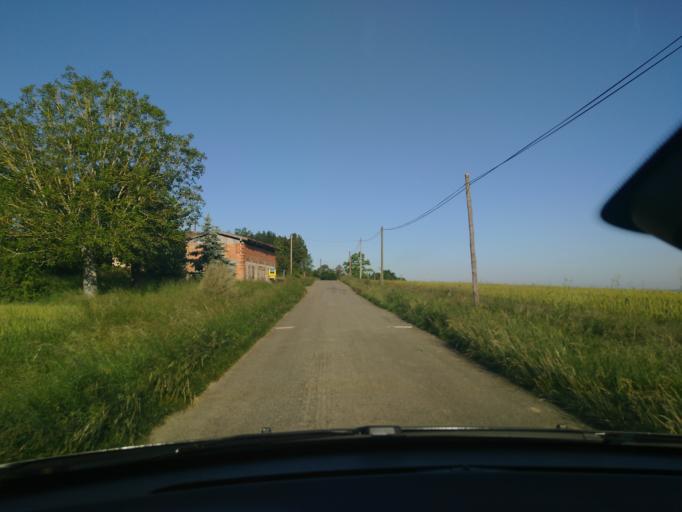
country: FR
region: Midi-Pyrenees
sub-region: Departement du Tarn-et-Garonne
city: Beaumont-de-Lomagne
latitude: 43.7816
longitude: 0.9794
